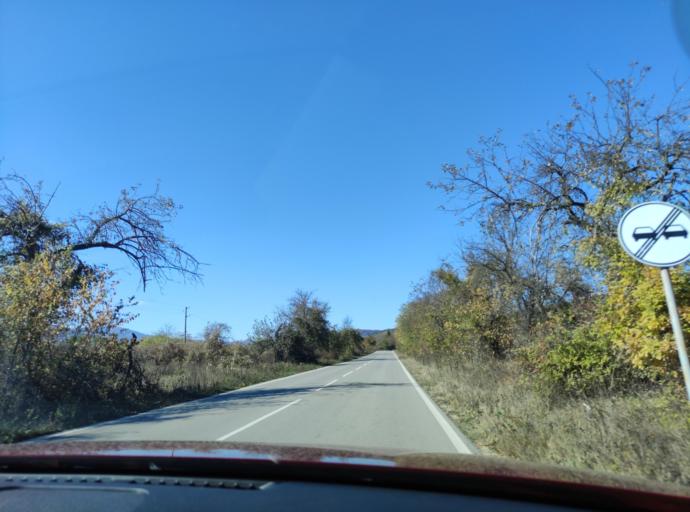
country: BG
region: Montana
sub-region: Obshtina Chiprovtsi
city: Chiprovtsi
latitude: 43.4204
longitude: 23.0200
